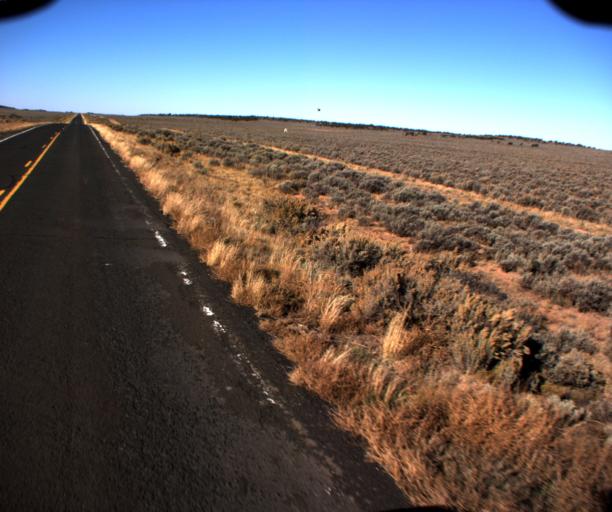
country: US
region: Arizona
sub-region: Navajo County
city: First Mesa
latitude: 35.7624
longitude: -110.0028
